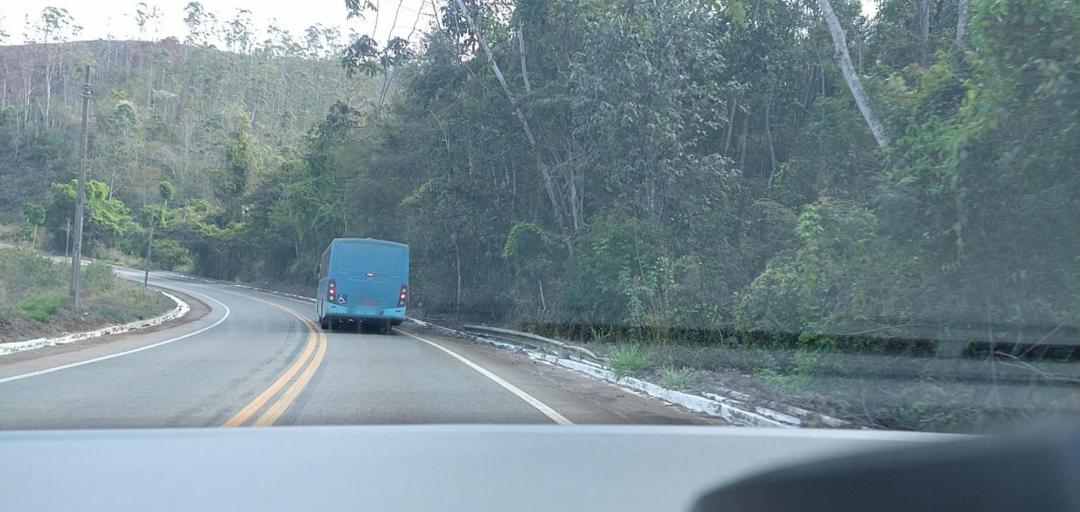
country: BR
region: Minas Gerais
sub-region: Rio Piracicaba
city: Rio Piracicaba
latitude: -19.8698
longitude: -43.1226
